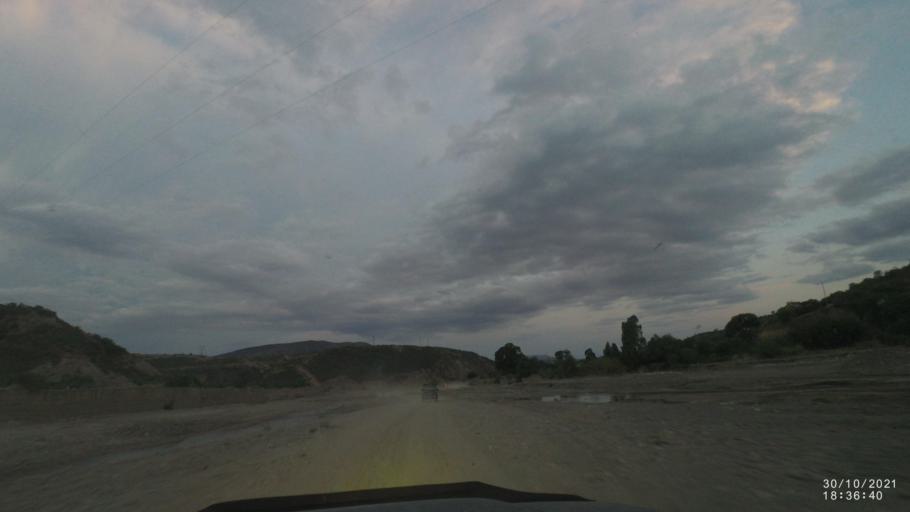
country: BO
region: Cochabamba
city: Sipe Sipe
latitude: -17.5721
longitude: -66.3603
